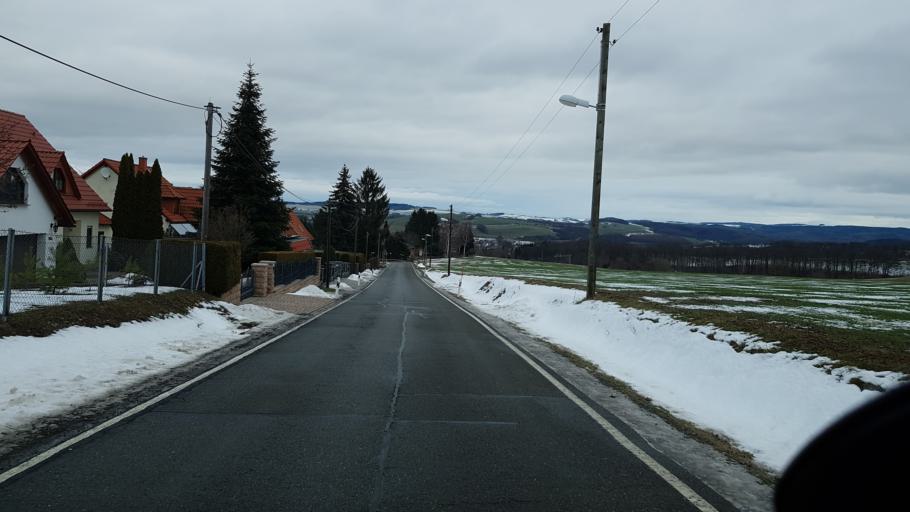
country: DE
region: Saxony
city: Kirchberg
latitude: 50.6412
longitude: 12.5517
